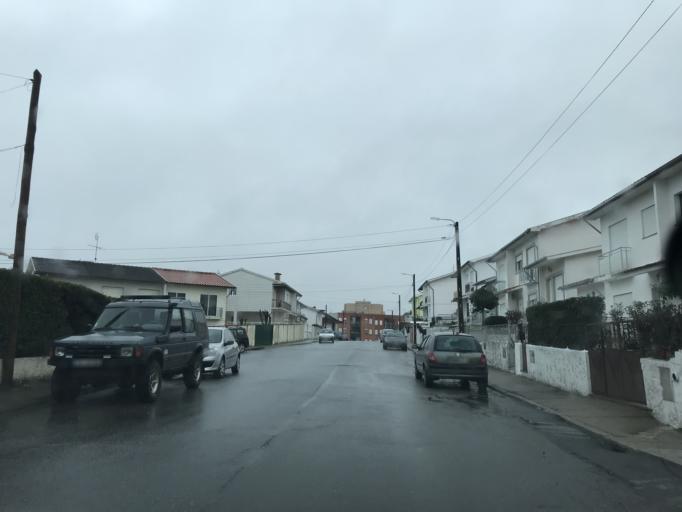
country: PT
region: Braga
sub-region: Vila Nova de Famalicao
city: Vila Nova de Famalicao
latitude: 41.4135
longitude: -8.5143
